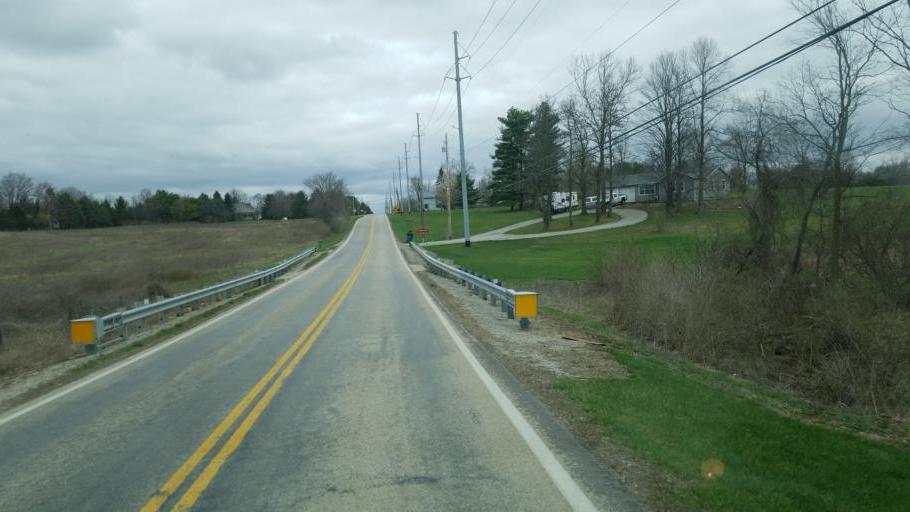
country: US
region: Ohio
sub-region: Delaware County
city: Delaware
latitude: 40.3471
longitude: -83.0989
